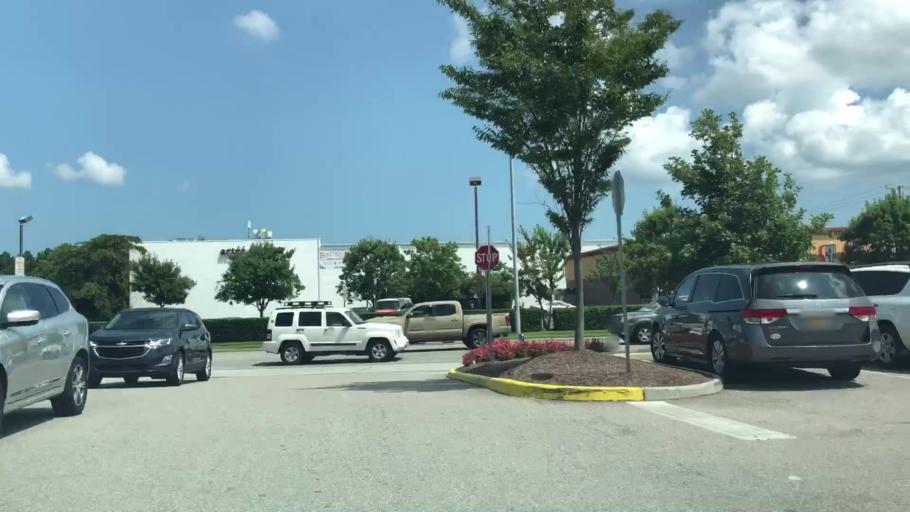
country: US
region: Virginia
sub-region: City of Virginia Beach
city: Virginia Beach
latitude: 36.8505
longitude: -76.0277
